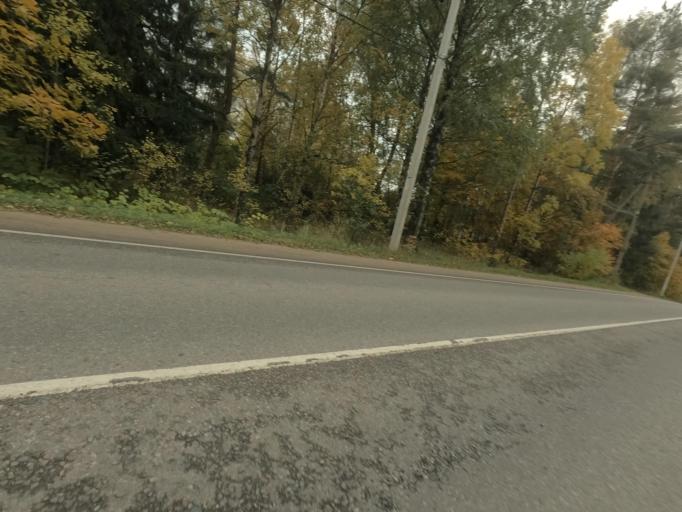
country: RU
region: Leningrad
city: Pavlovo
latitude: 59.7750
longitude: 30.9718
